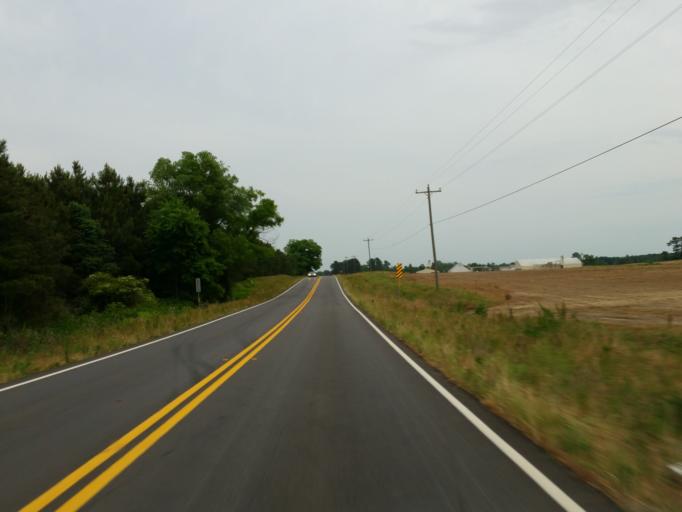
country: US
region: Georgia
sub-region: Dooly County
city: Unadilla
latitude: 32.2868
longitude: -83.7491
